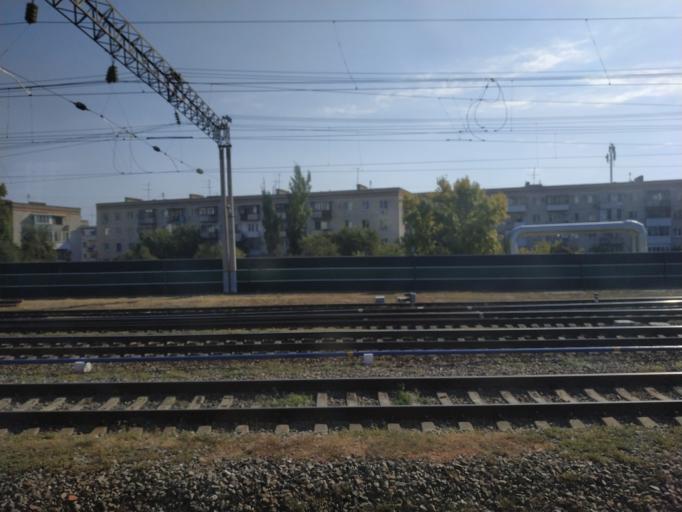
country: RU
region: Volgograd
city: Volgograd
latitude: 48.7229
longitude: 44.5277
